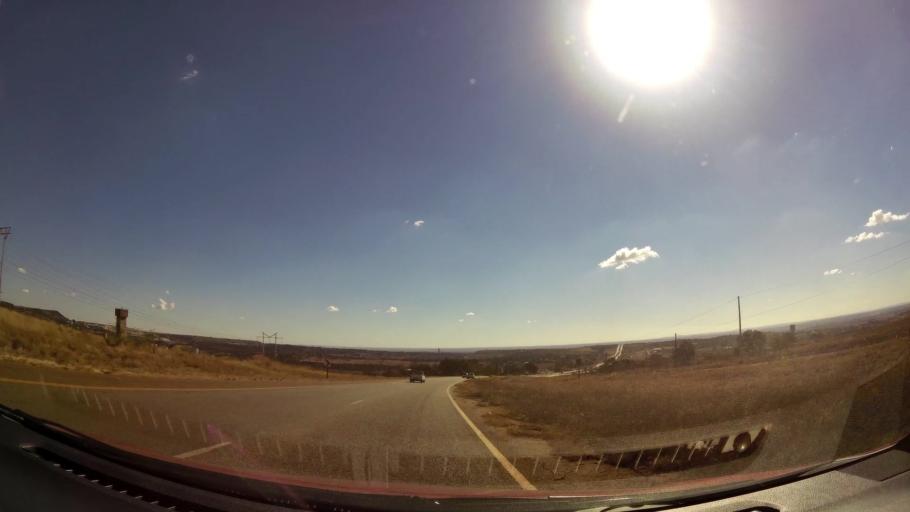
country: ZA
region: Gauteng
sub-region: West Rand District Municipality
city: Carletonville
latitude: -26.4151
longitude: 27.4348
